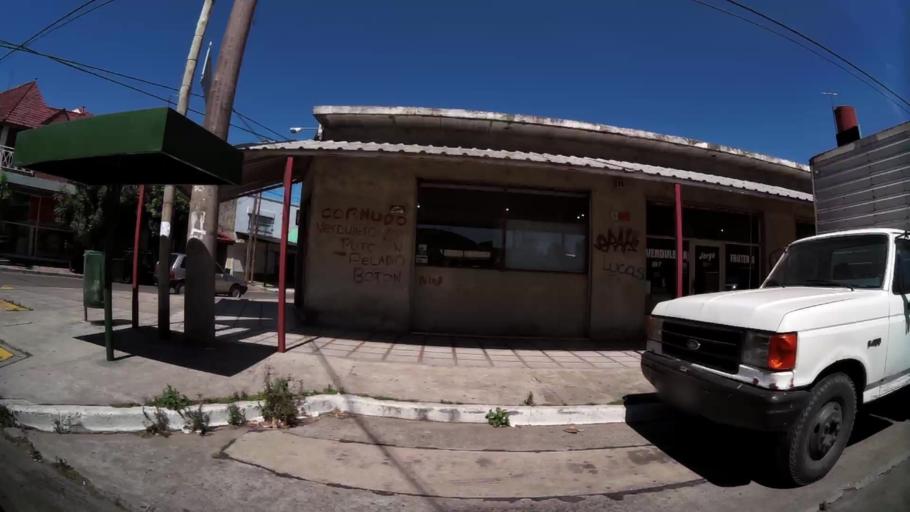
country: AR
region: Buenos Aires
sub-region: Partido de Tigre
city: Tigre
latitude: -34.4971
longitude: -58.6153
